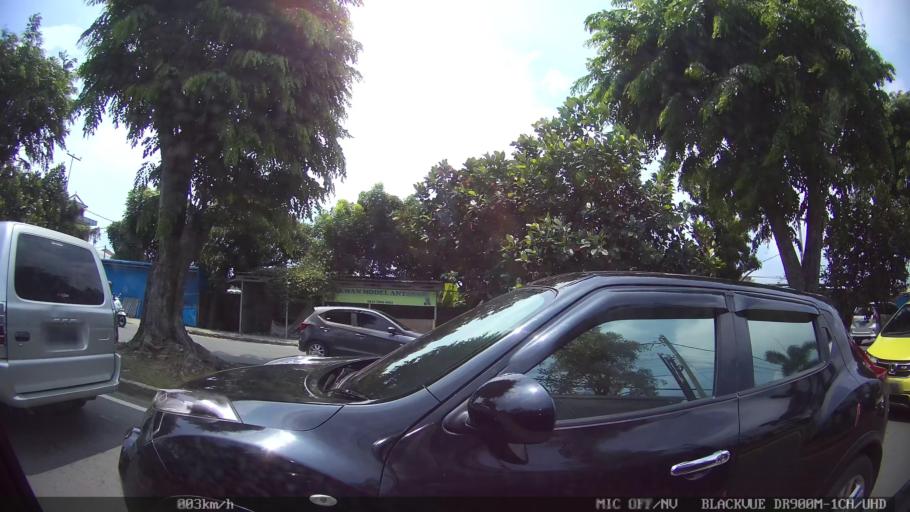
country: ID
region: Lampung
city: Kedaton
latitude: -5.3809
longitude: 105.2732
